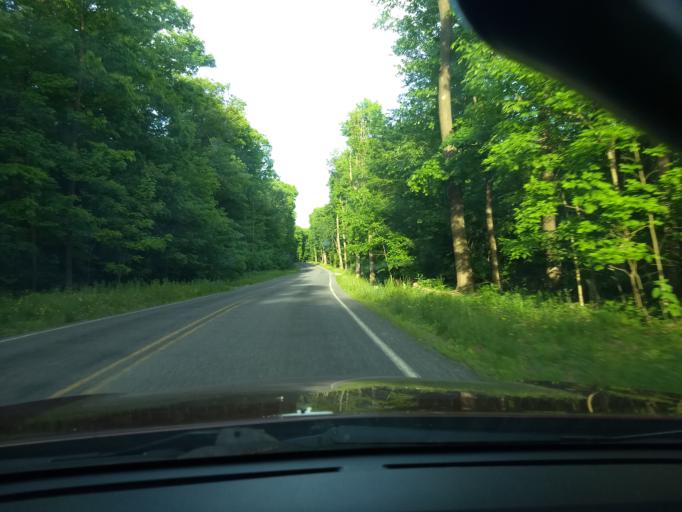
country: US
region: Pennsylvania
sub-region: Cambria County
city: Gallitzin
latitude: 40.5128
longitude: -78.5329
